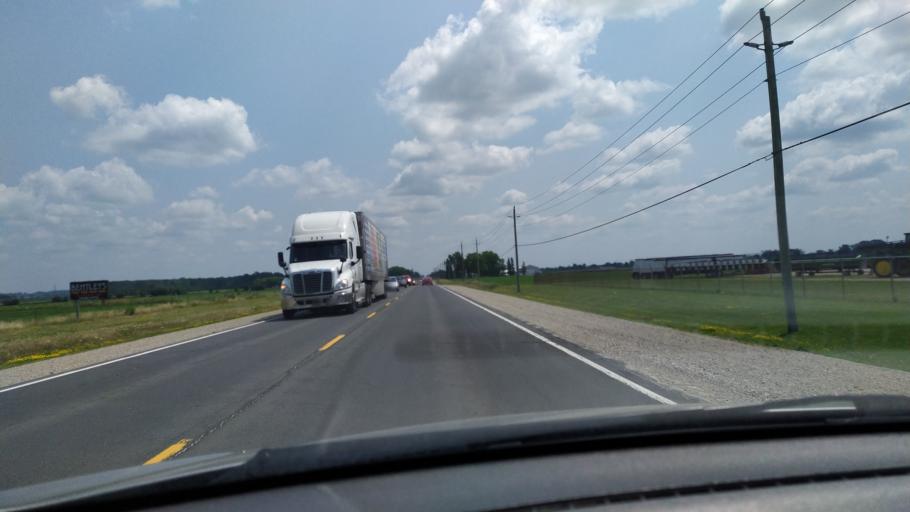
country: CA
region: Ontario
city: Stratford
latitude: 43.3701
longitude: -80.8990
